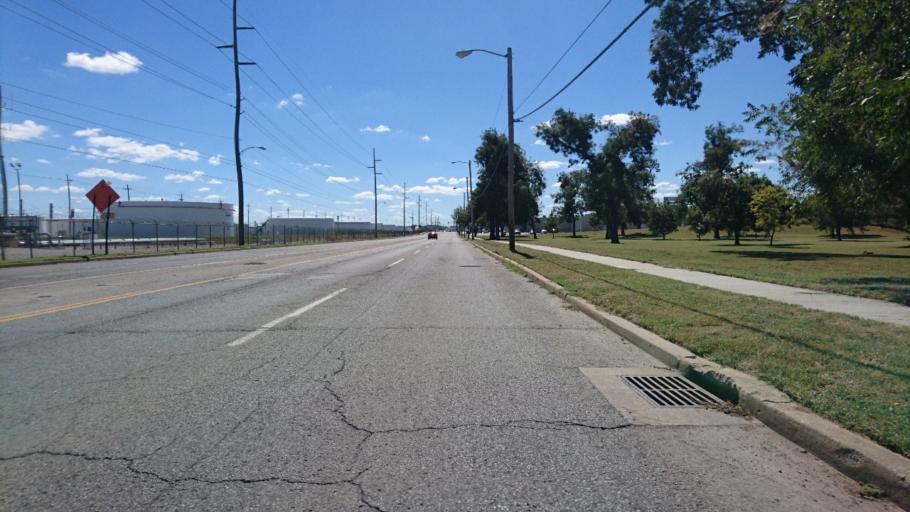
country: US
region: Oklahoma
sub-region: Tulsa County
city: Tulsa
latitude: 36.1253
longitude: -96.0072
